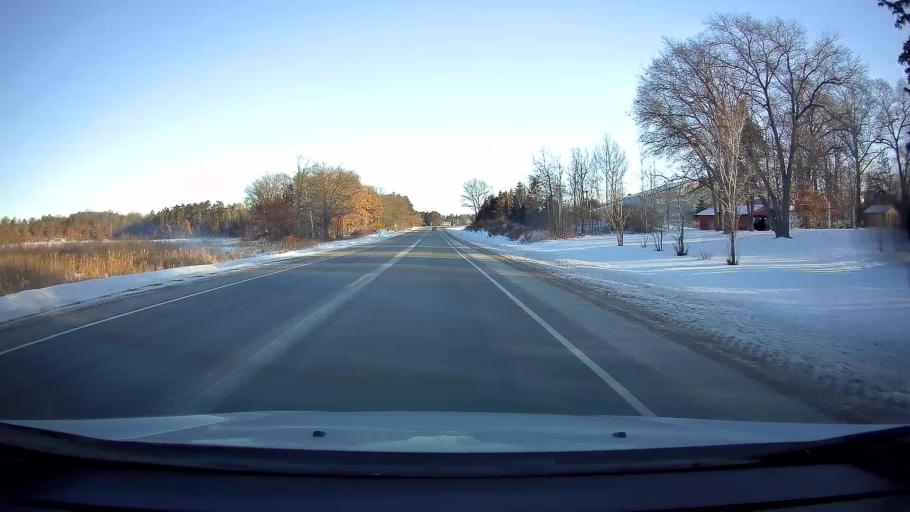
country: US
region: Wisconsin
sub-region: Washburn County
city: Spooner
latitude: 45.8365
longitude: -91.8816
